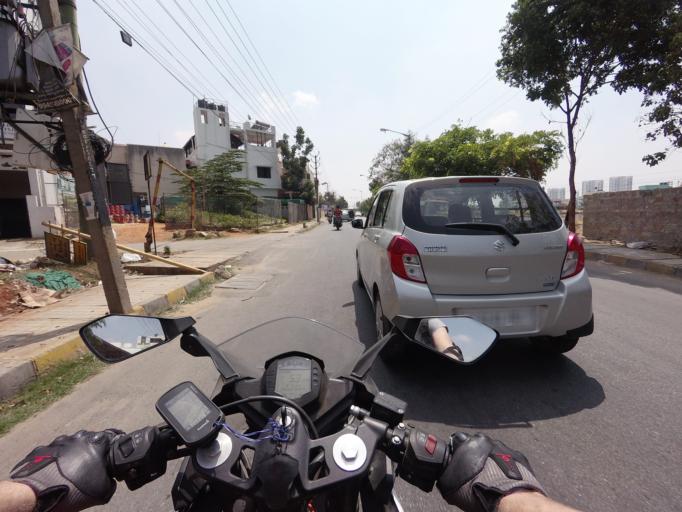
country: IN
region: Karnataka
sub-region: Bangalore Urban
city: Bangalore
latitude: 12.9961
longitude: 77.6610
